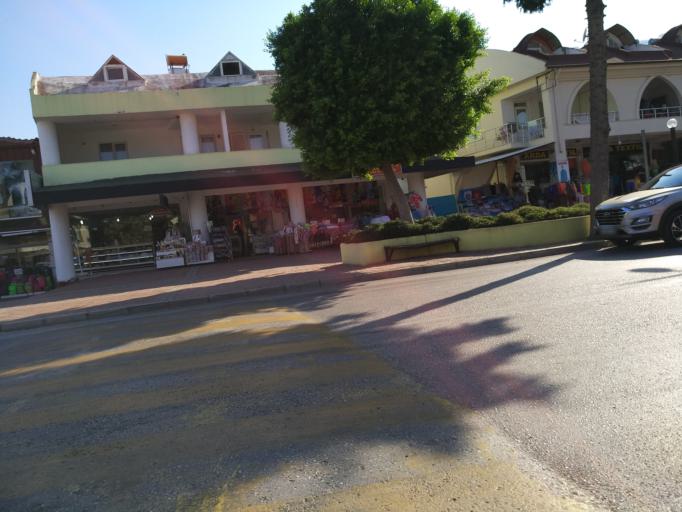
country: TR
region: Antalya
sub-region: Kemer
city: Goeynuek
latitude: 36.6652
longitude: 30.5547
